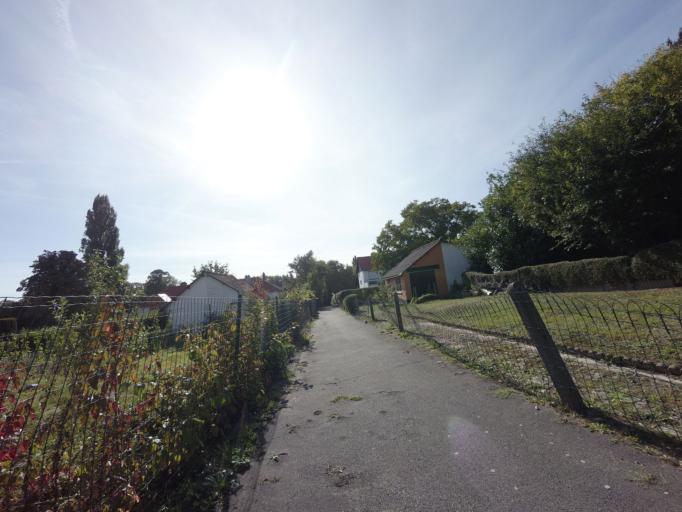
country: BE
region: Flanders
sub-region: Provincie Vlaams-Brabant
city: Kraainem
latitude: 50.8696
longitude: 4.4471
